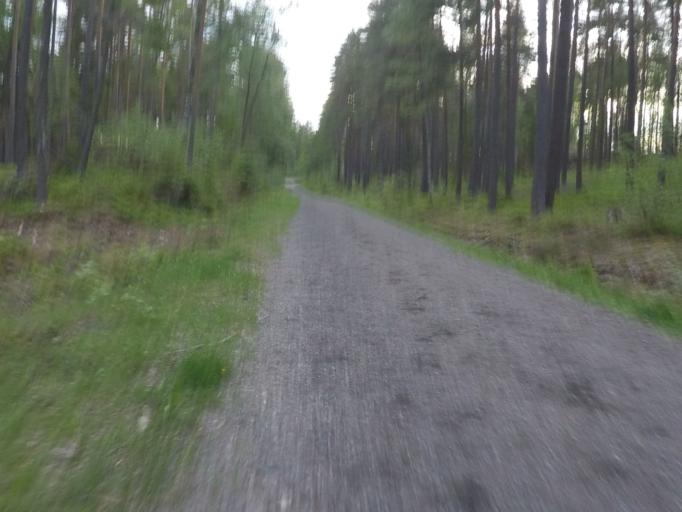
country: SE
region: Soedermanland
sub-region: Eskilstuna Kommun
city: Kvicksund
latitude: 59.4065
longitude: 16.2751
